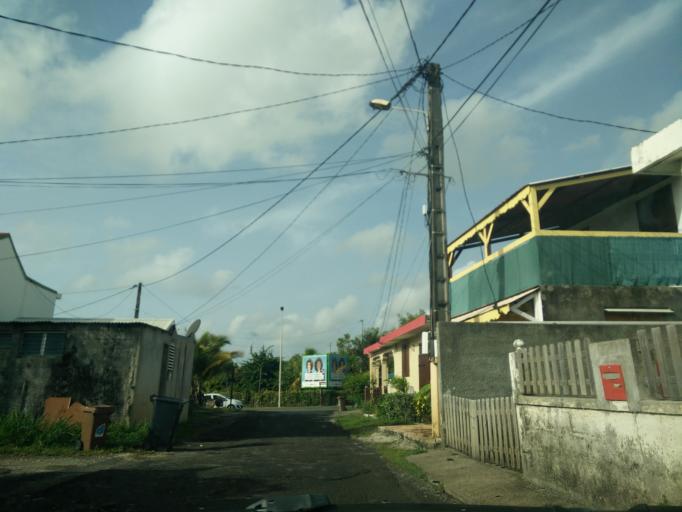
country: GP
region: Guadeloupe
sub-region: Guadeloupe
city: Le Moule
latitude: 16.3246
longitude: -61.3457
